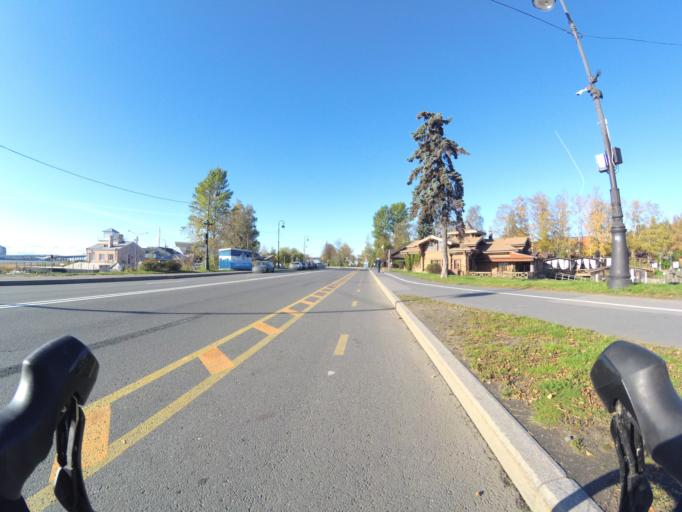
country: RU
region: St.-Petersburg
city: Staraya Derevnya
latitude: 59.9690
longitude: 30.2342
